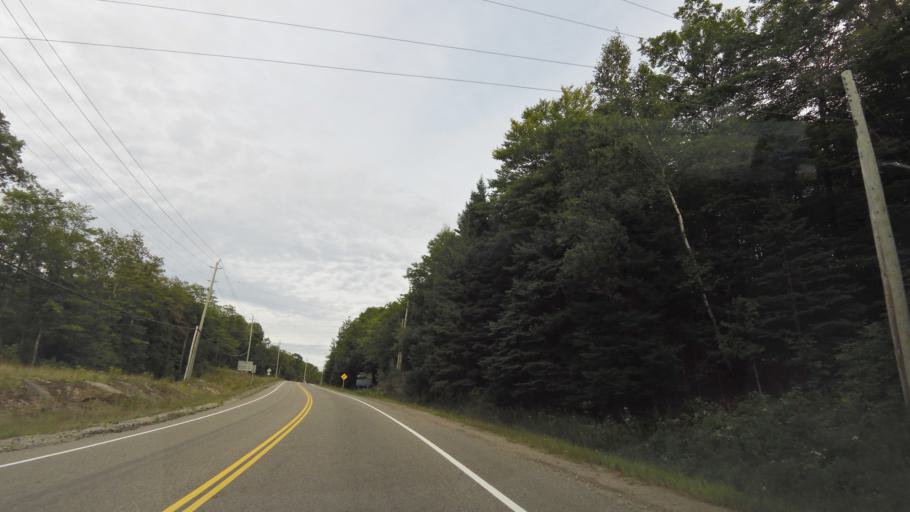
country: CA
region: Ontario
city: Bancroft
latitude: 45.0402
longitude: -78.4826
